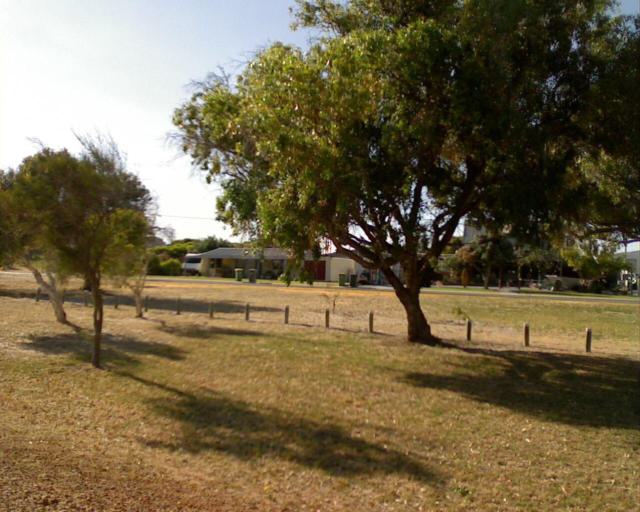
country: AU
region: Western Australia
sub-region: Dandaragan
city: Jurien Bay
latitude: -30.0679
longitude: 114.9715
